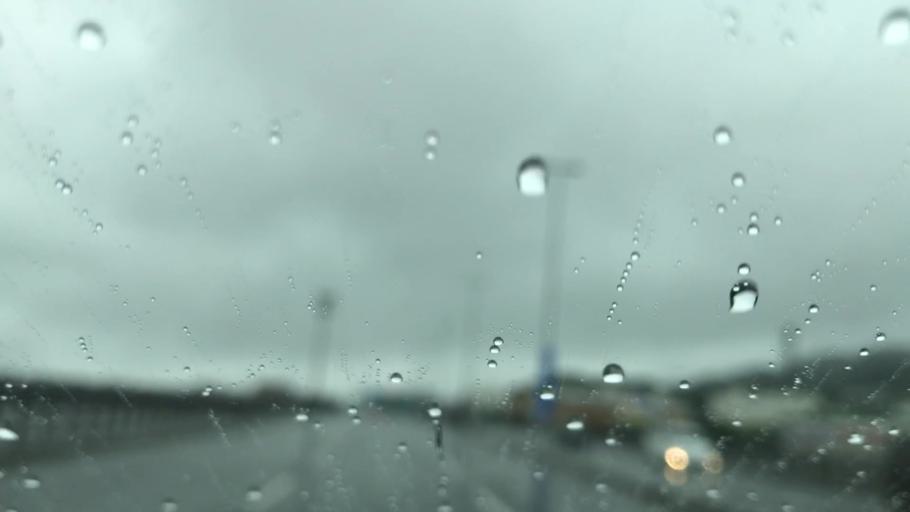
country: JP
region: Hokkaido
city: Otaru
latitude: 43.1848
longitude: 141.0165
